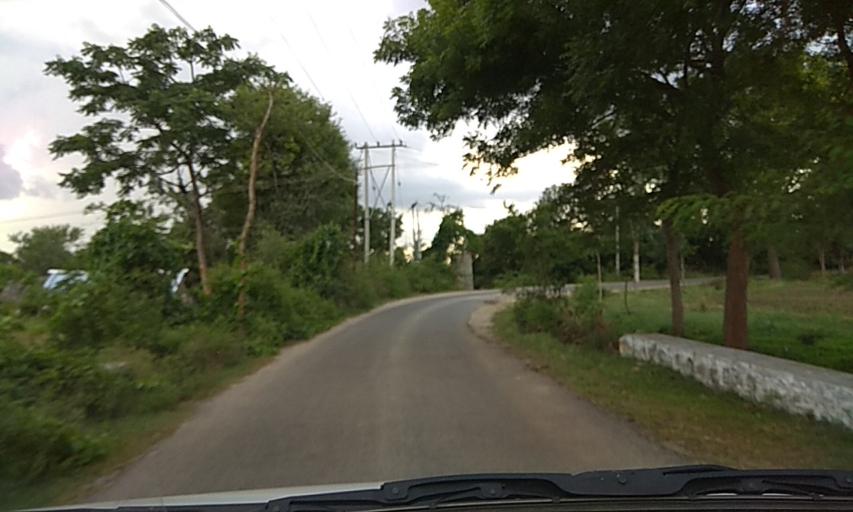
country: IN
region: Karnataka
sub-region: Chamrajnagar
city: Gundlupet
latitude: 11.8709
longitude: 76.7328
